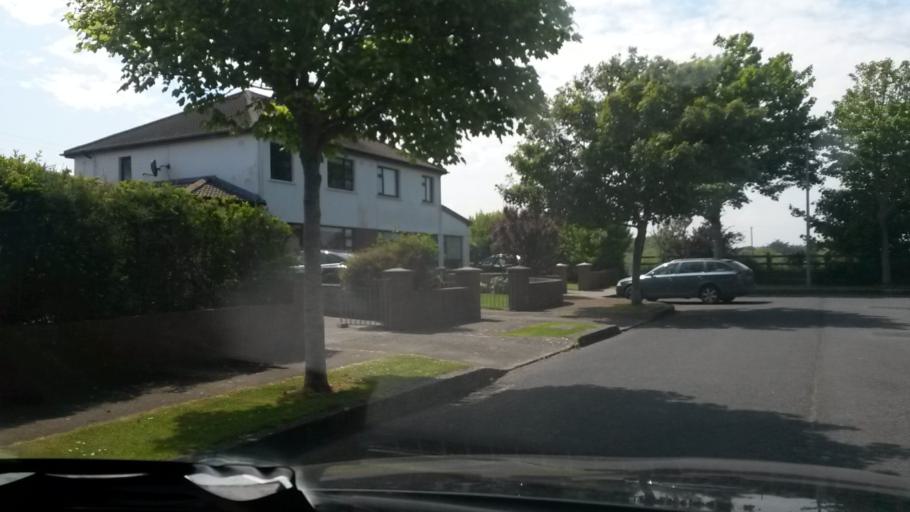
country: IE
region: Leinster
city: Portraine
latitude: 53.4913
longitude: -6.1075
